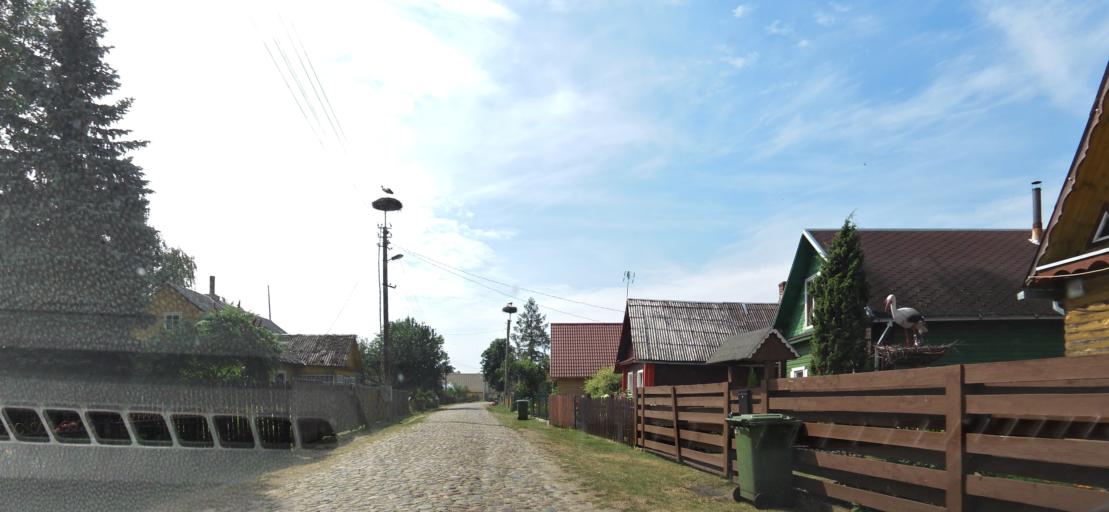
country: LT
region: Vilnius County
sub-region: Trakai
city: Rudiskes
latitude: 54.3652
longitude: 24.8456
